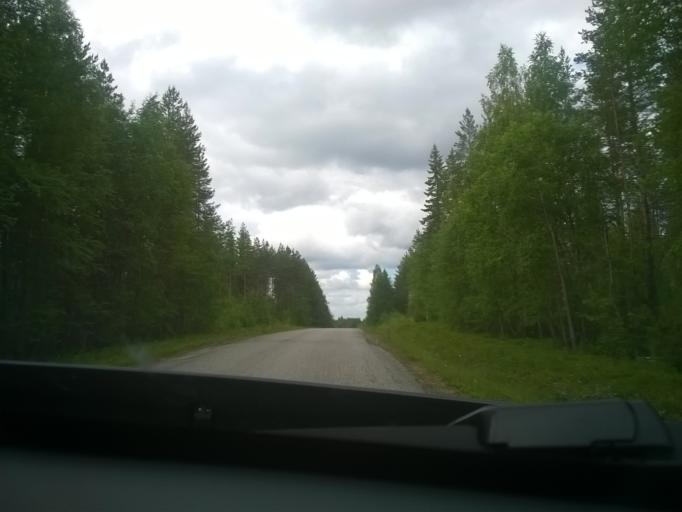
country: FI
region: Kainuu
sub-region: Kehys-Kainuu
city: Kuhmo
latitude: 64.3895
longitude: 29.7875
